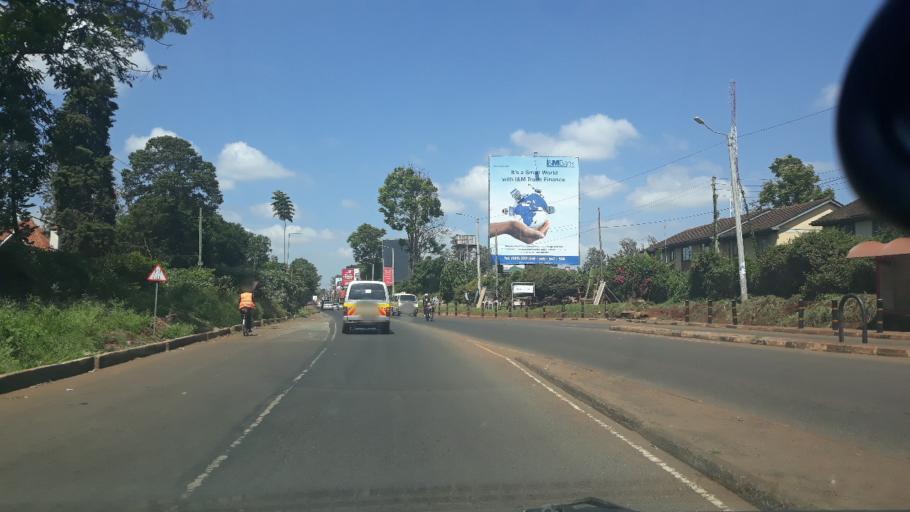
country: KE
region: Nairobi Area
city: Nairobi
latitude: -1.2380
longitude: 36.8098
